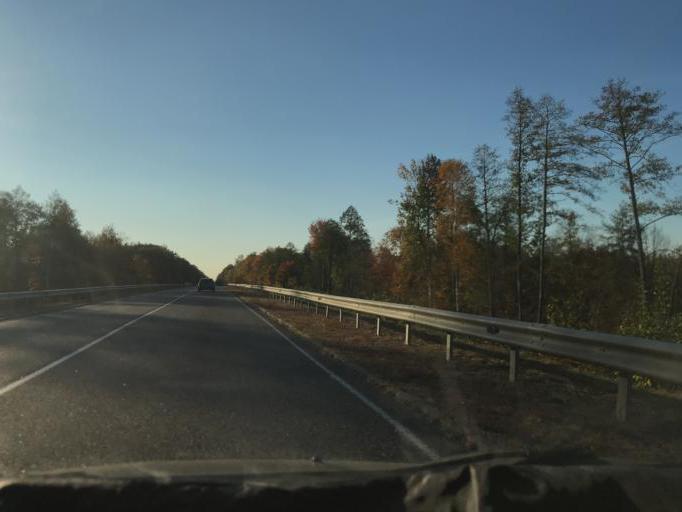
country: BY
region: Gomel
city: Zhytkavichy
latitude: 52.2738
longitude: 28.1303
